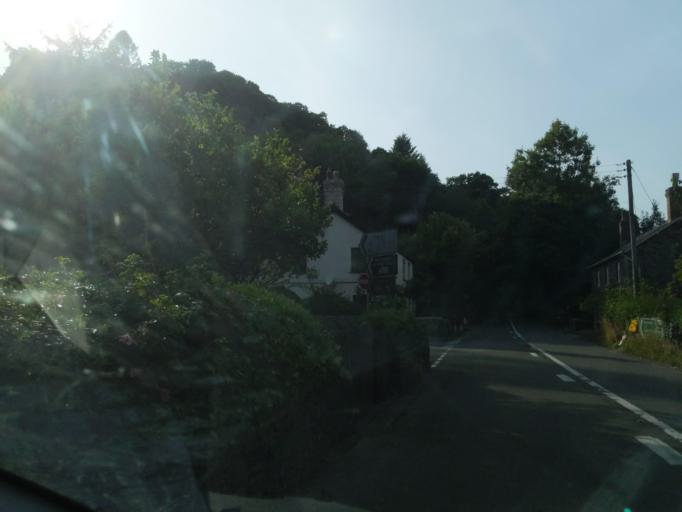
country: GB
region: England
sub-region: Devon
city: Winkleigh
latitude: 50.9556
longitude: -3.9610
